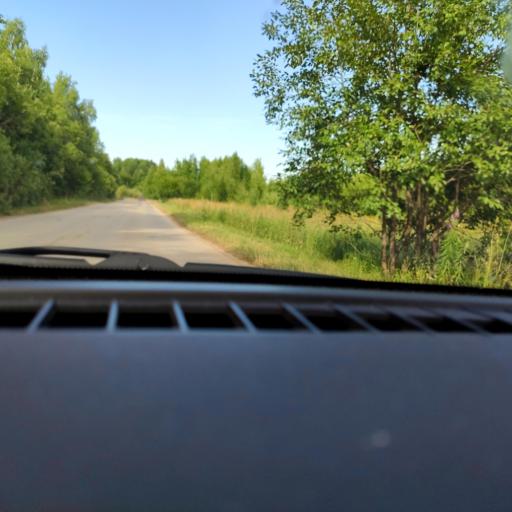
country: RU
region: Perm
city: Polazna
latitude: 58.3593
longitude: 56.2475
